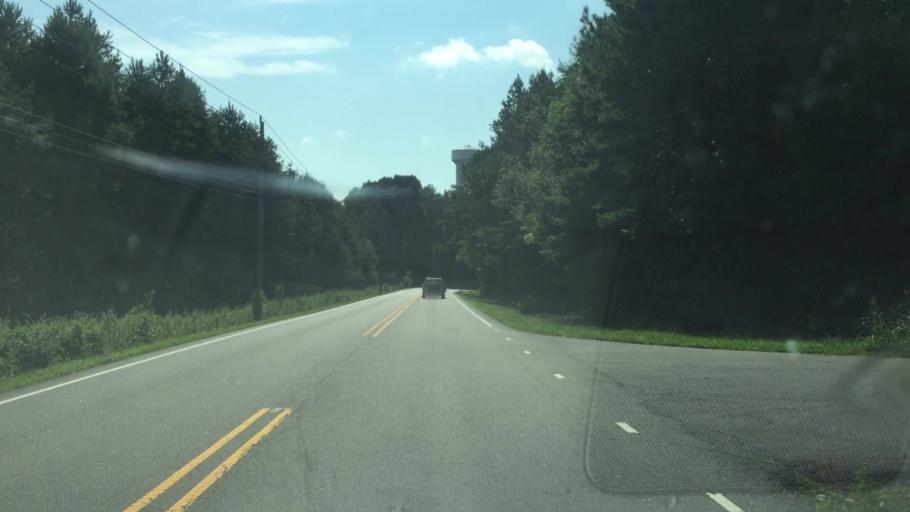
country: US
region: North Carolina
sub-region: Mecklenburg County
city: Mint Hill
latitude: 35.1651
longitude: -80.5902
